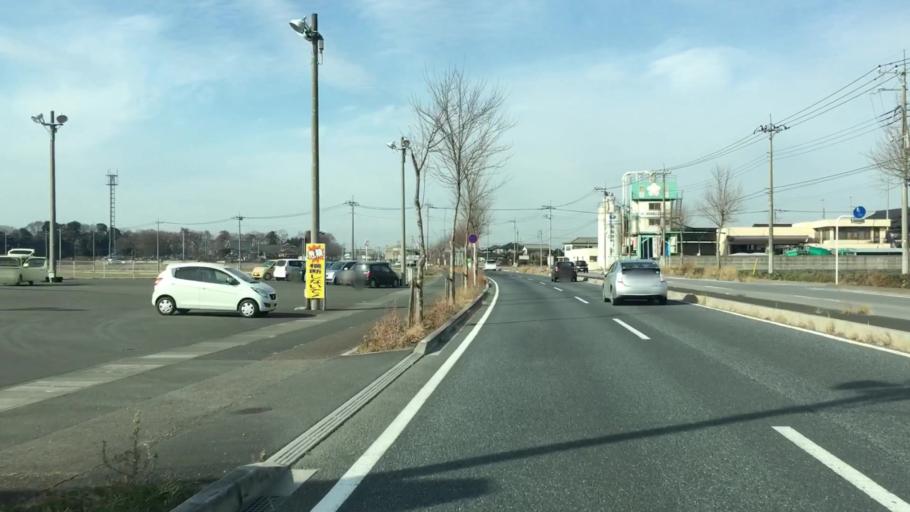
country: JP
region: Gunma
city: Tatebayashi
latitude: 36.2368
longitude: 139.4757
